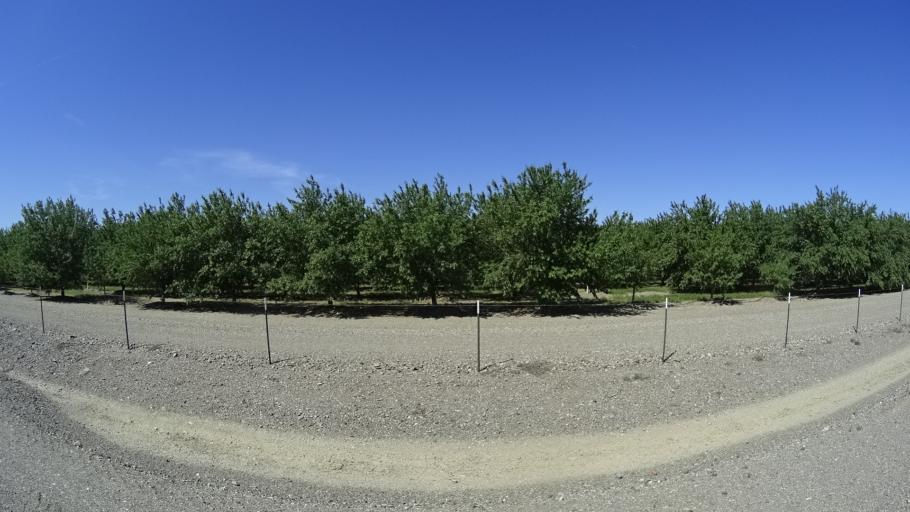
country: US
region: California
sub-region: Glenn County
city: Orland
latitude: 39.7279
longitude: -122.1410
